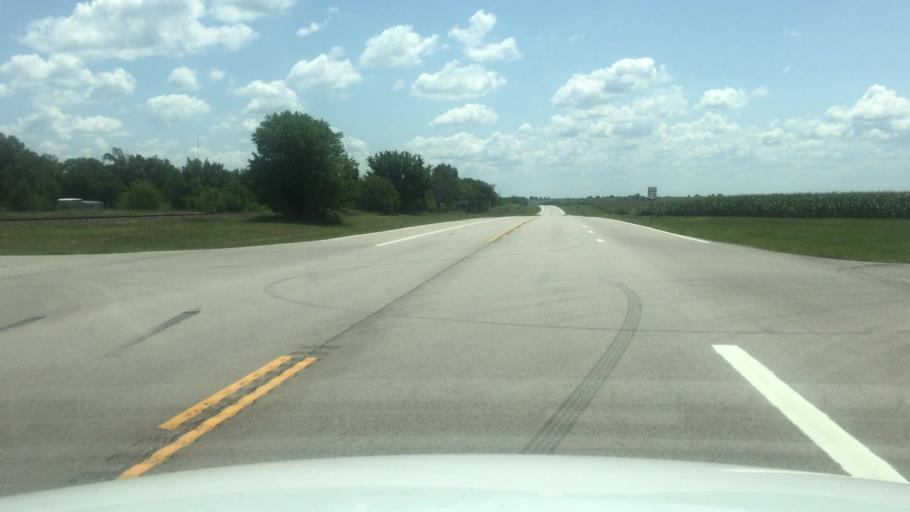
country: US
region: Kansas
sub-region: Brown County
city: Horton
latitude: 39.6385
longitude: -95.3533
